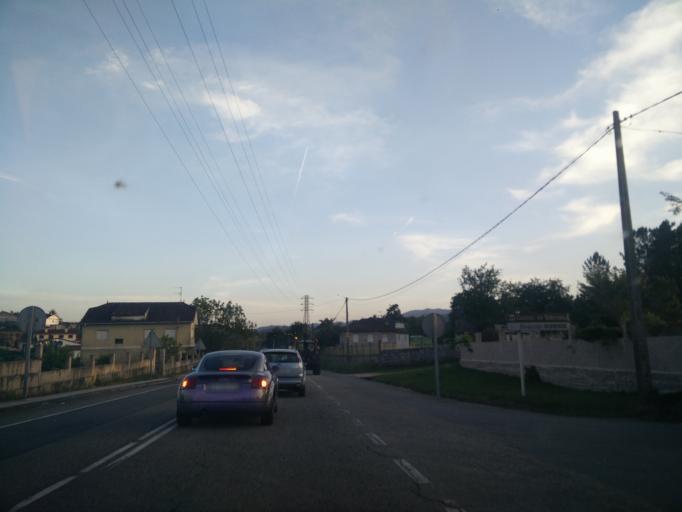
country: ES
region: Galicia
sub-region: Provincia de Pontevedra
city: Ponteareas
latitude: 42.1822
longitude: -8.5075
